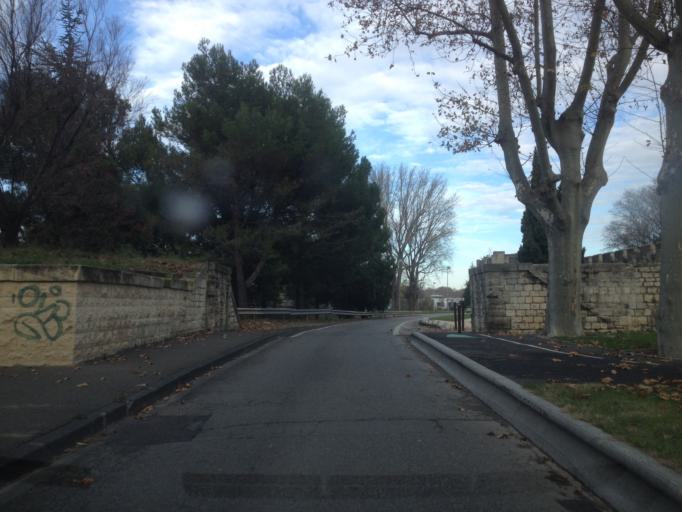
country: FR
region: Provence-Alpes-Cote d'Azur
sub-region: Departement du Vaucluse
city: Avignon
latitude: 43.9446
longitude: 4.7979
